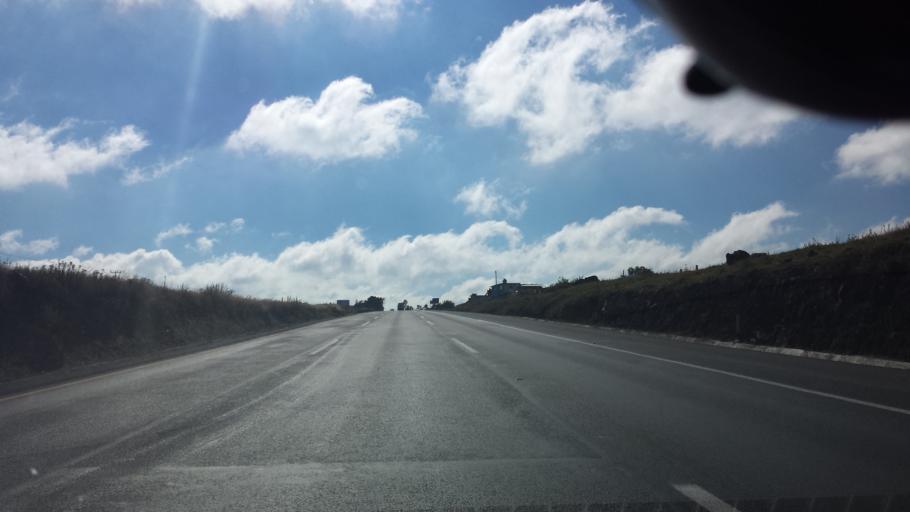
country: MX
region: Mexico
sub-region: Jilotepec
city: San Vicente (Calpulalpan Tercera Manzana)
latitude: 20.0935
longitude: -99.6889
